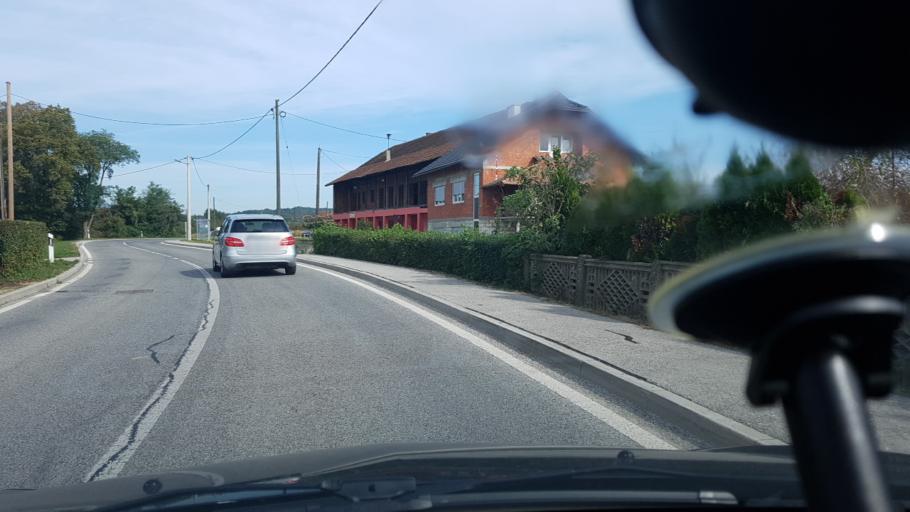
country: HR
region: Krapinsko-Zagorska
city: Marija Bistrica
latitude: 46.0740
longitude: 16.1913
